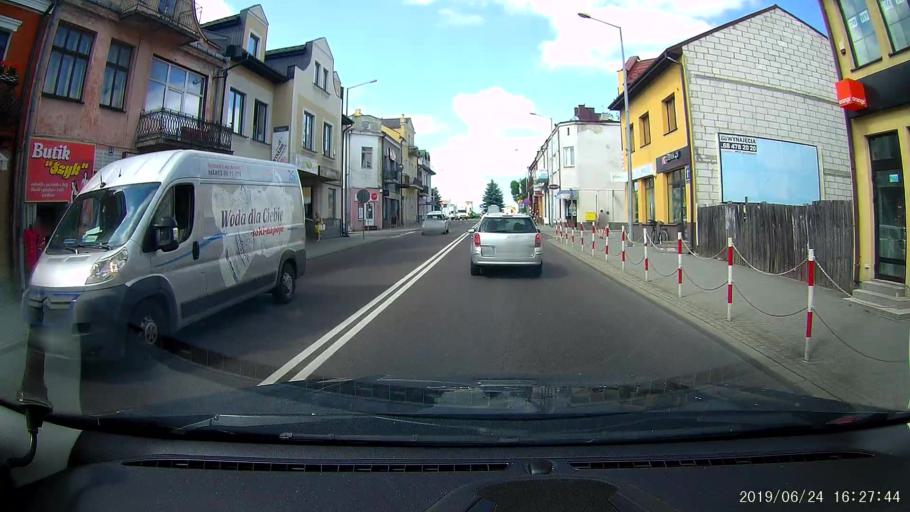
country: PL
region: Lublin Voivodeship
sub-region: Powiat tomaszowski
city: Tomaszow Lubelski
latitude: 50.4520
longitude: 23.4186
